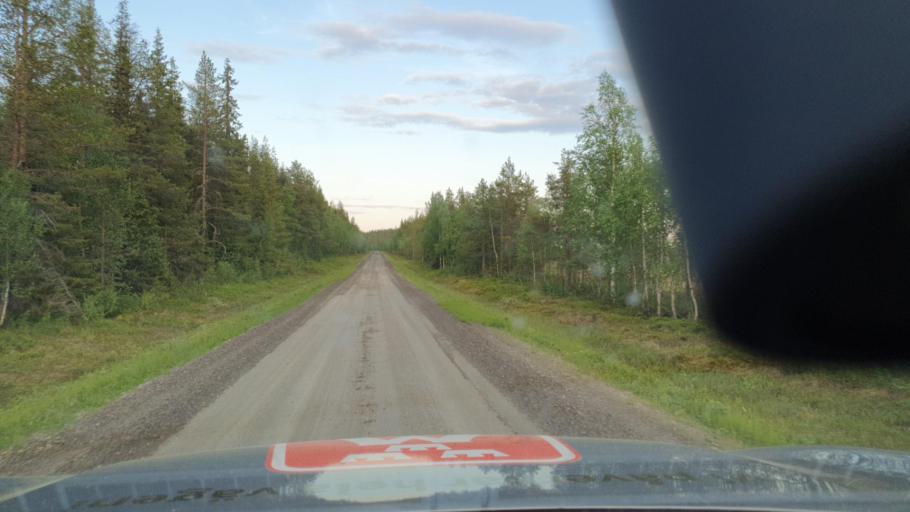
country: SE
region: Norrbotten
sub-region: Bodens Kommun
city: Boden
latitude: 66.5212
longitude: 21.5035
